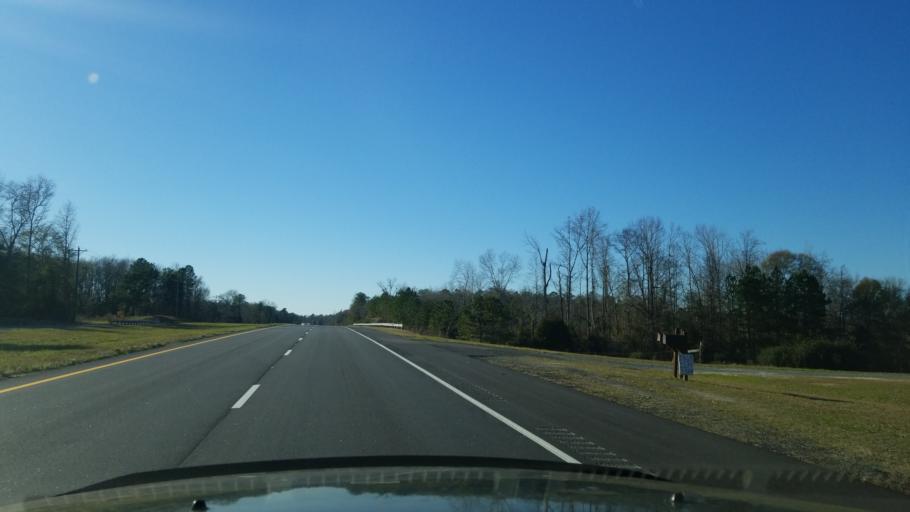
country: US
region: Georgia
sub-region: Talbot County
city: Talbotton
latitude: 32.5751
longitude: -84.5776
